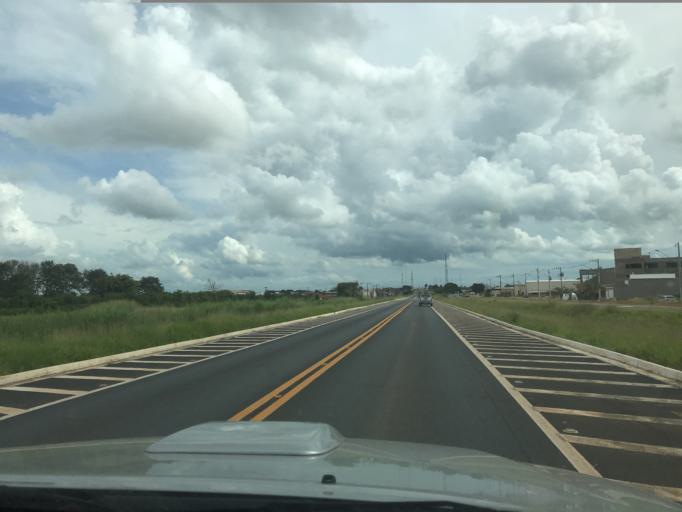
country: BR
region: Minas Gerais
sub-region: Patrocinio
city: Patrocinio
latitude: -19.1008
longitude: -46.6763
